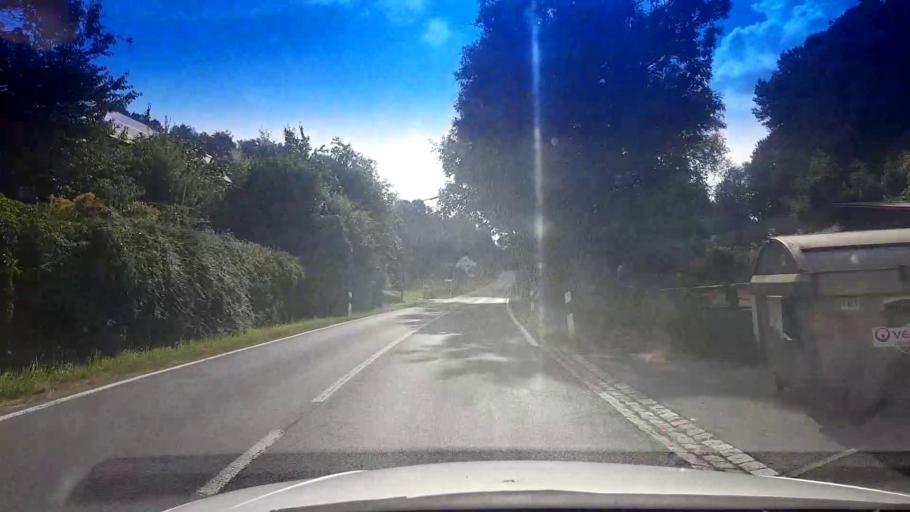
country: DE
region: Bavaria
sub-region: Upper Franconia
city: Mistelgau
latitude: 49.9373
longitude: 11.4091
